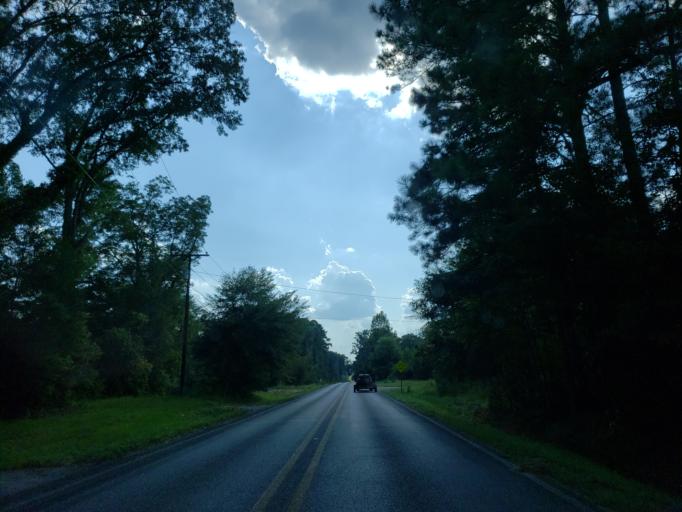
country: US
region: Mississippi
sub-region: Jones County
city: Sharon
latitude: 31.9198
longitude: -89.0227
